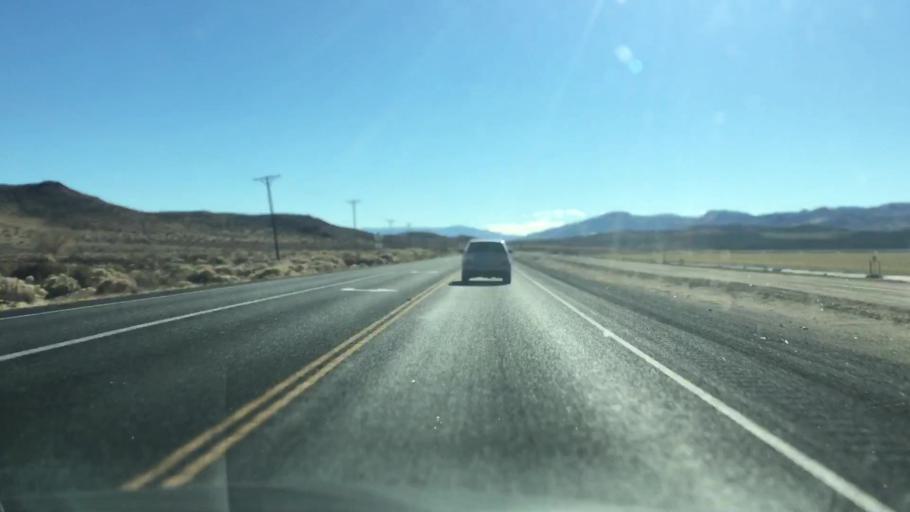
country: US
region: Nevada
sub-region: Lyon County
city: Yerington
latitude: 39.0256
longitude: -119.1817
